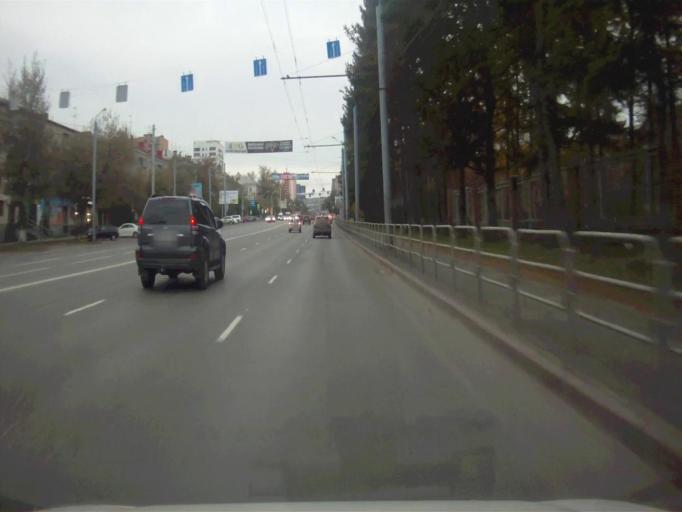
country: RU
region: Chelyabinsk
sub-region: Gorod Chelyabinsk
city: Chelyabinsk
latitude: 55.1645
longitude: 61.3807
